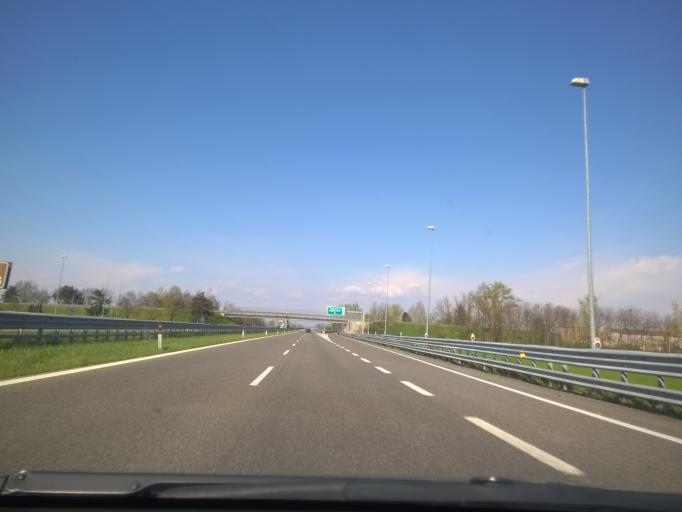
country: IT
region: Lombardy
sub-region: Provincia di Brescia
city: Alfianello
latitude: 45.2708
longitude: 10.1289
